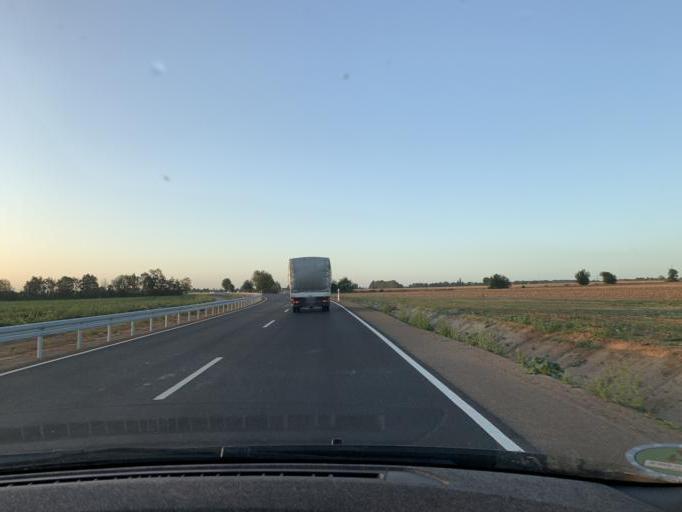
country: DE
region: North Rhine-Westphalia
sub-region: Regierungsbezirk Koln
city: Vettweiss
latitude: 50.7264
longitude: 6.5724
